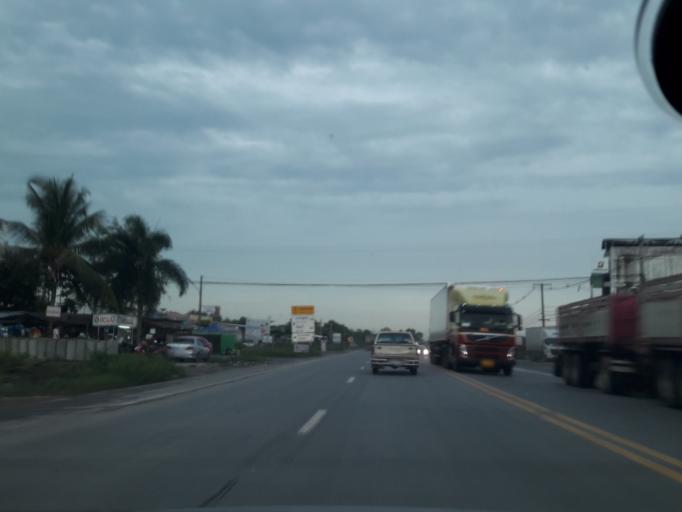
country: TH
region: Pathum Thani
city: Ban Rangsit
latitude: 14.0484
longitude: 100.7485
